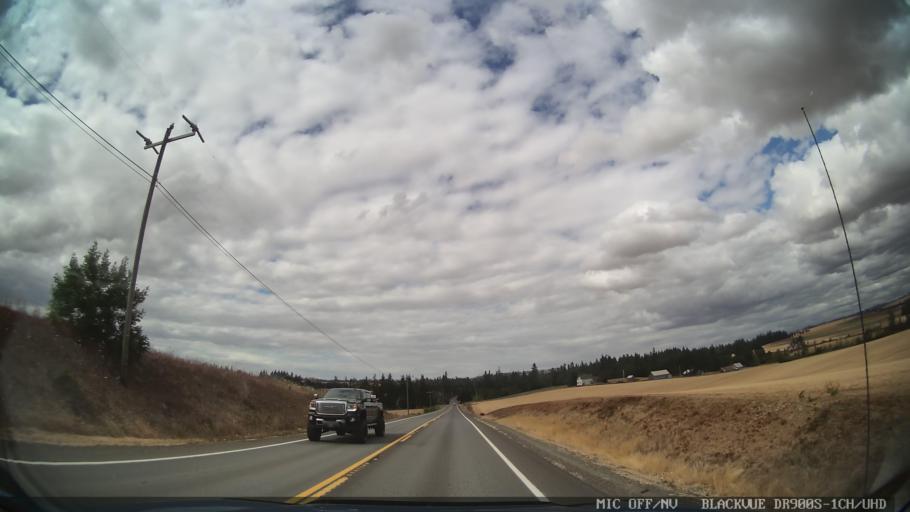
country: US
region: Oregon
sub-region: Marion County
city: Sublimity
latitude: 44.8431
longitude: -122.7945
